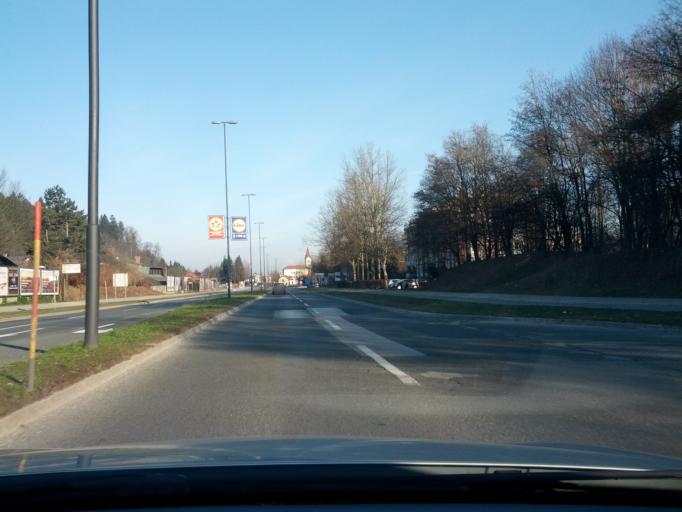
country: SI
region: Ljubljana
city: Ljubljana
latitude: 46.0910
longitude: 14.4710
